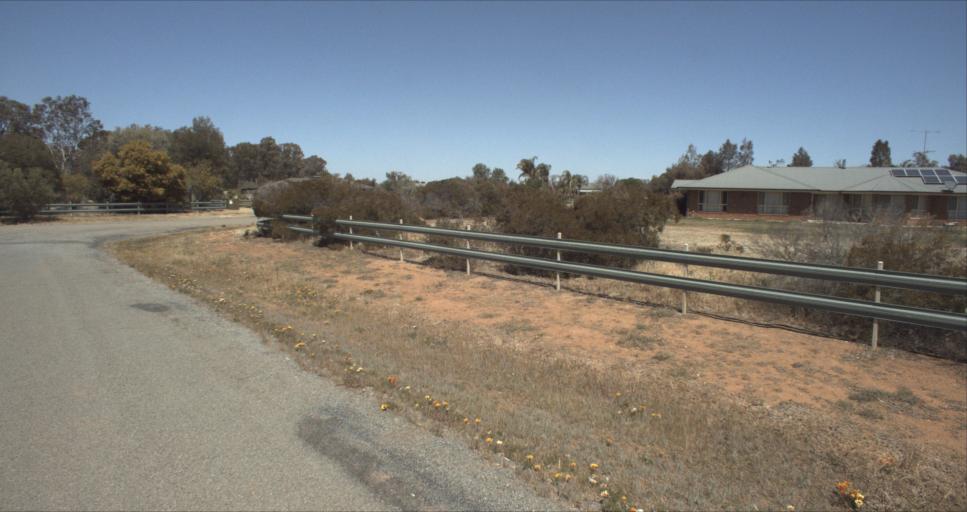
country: AU
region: New South Wales
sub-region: Leeton
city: Leeton
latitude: -34.5303
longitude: 146.3958
